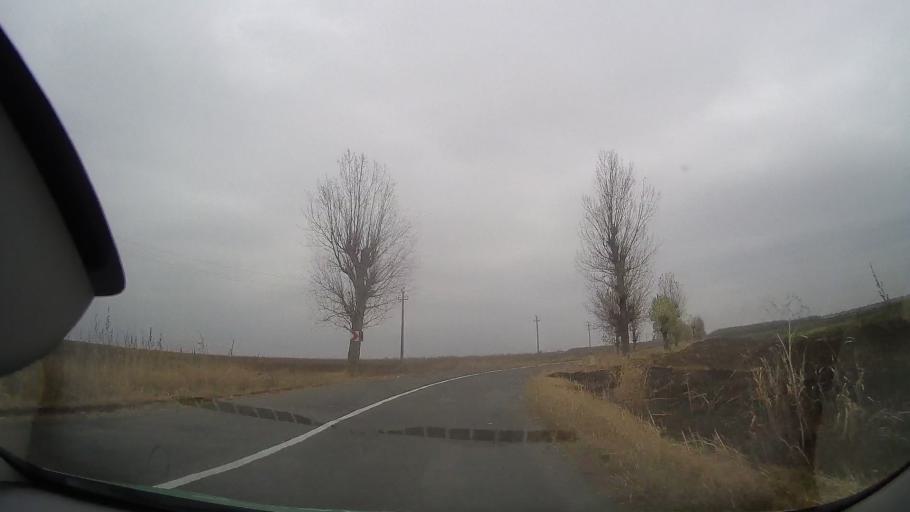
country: RO
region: Ialomita
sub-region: Comuna Grindu
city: Grindu
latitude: 44.7918
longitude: 26.8998
